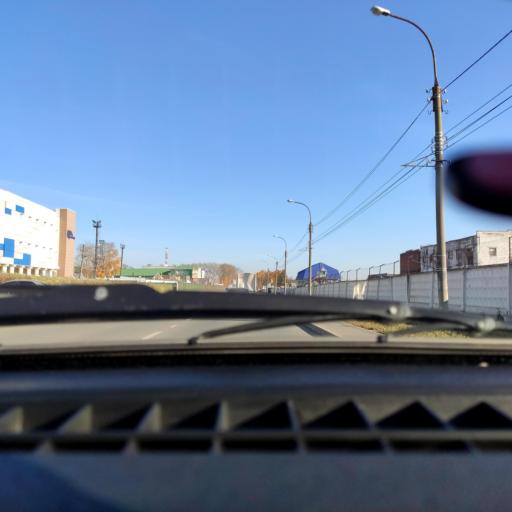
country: RU
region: Bashkortostan
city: Ufa
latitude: 54.8053
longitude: 56.0903
